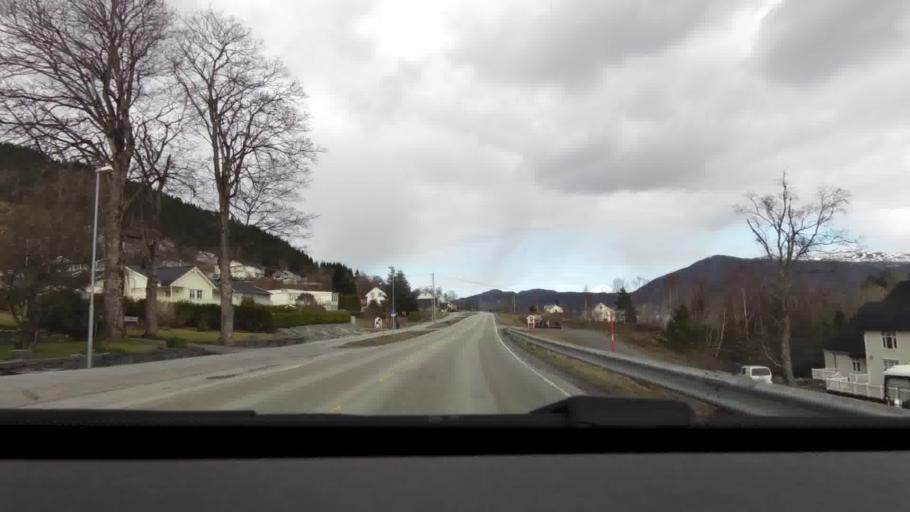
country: NO
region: More og Romsdal
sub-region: Eide
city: Eide
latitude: 62.9239
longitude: 7.4474
